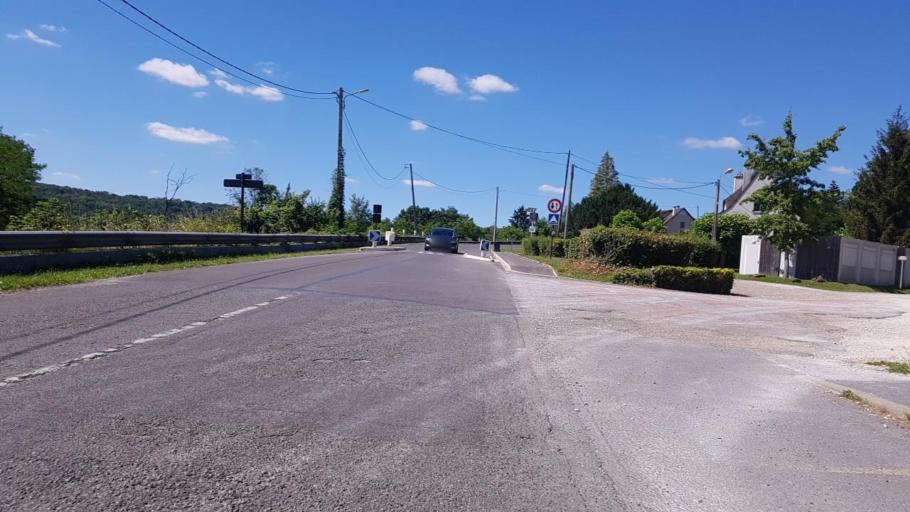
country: FR
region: Ile-de-France
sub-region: Departement de Seine-et-Marne
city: Saacy-sur-Marne
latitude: 48.9654
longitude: 3.2028
